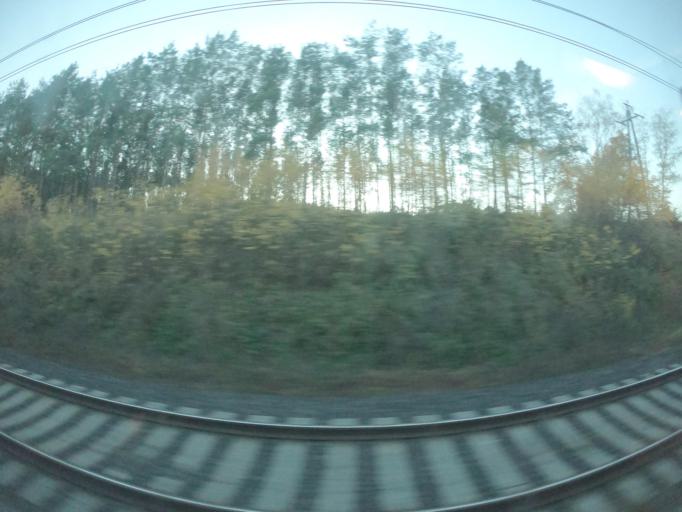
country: PL
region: West Pomeranian Voivodeship
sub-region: Powiat mysliborski
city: Boleszkowice
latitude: 52.7241
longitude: 14.5262
